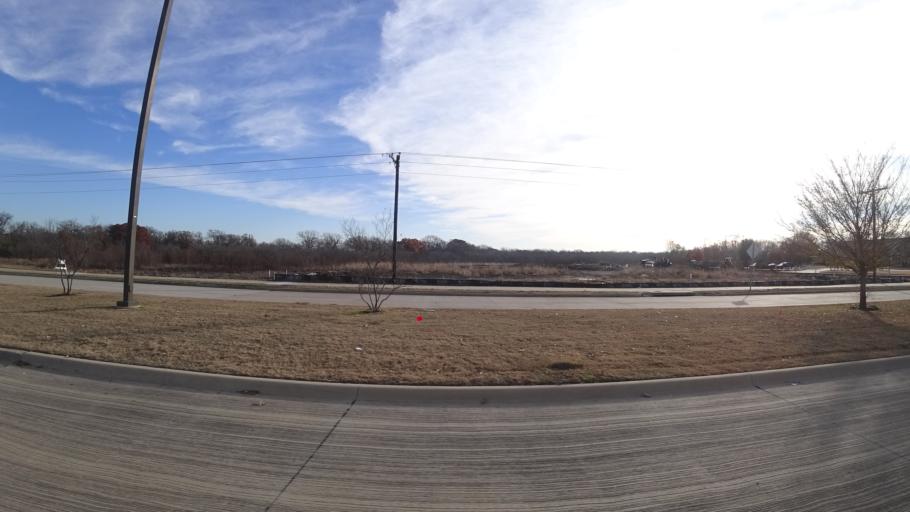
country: US
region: Texas
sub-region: Collin County
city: McKinney
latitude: 33.2079
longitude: -96.6798
